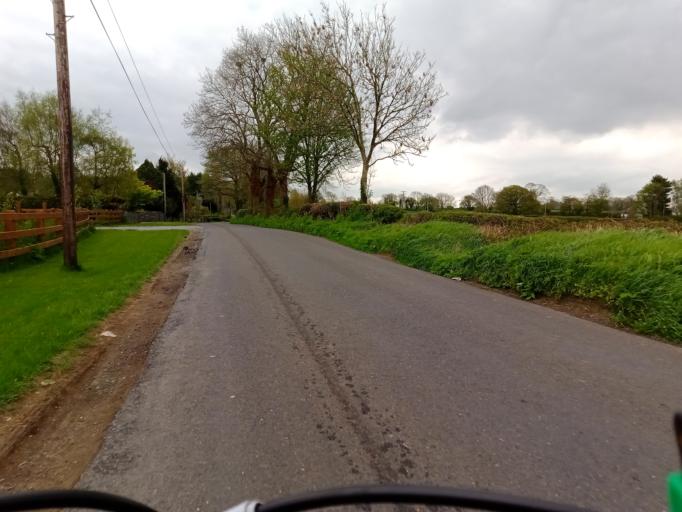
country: IE
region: Leinster
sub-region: Kilkenny
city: Kilkenny
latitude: 52.6204
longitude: -7.2773
